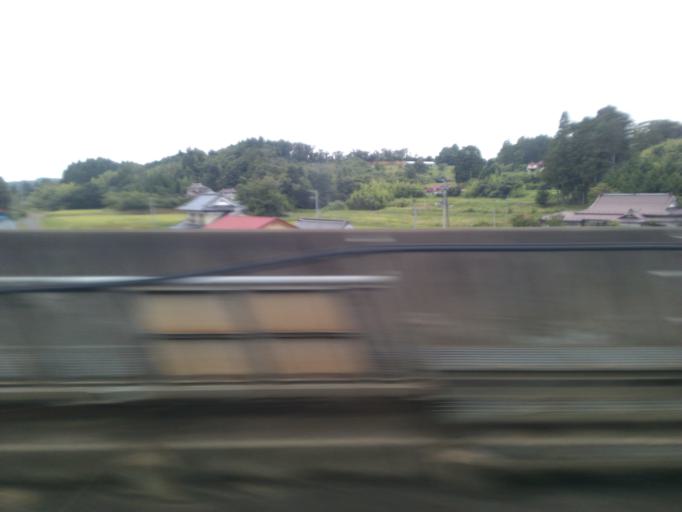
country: JP
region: Miyagi
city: Kogota
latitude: 38.7050
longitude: 141.0469
